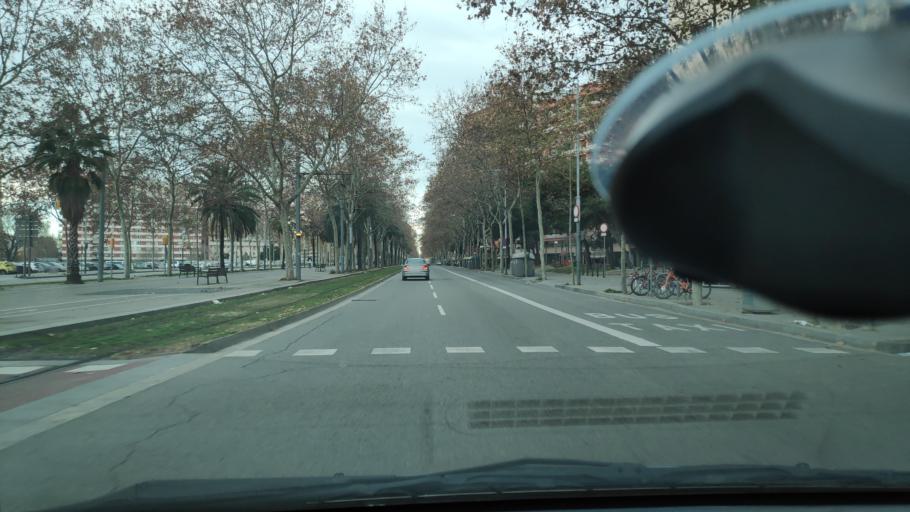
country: ES
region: Catalonia
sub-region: Provincia de Barcelona
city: Sant Marti
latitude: 41.4102
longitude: 2.2138
